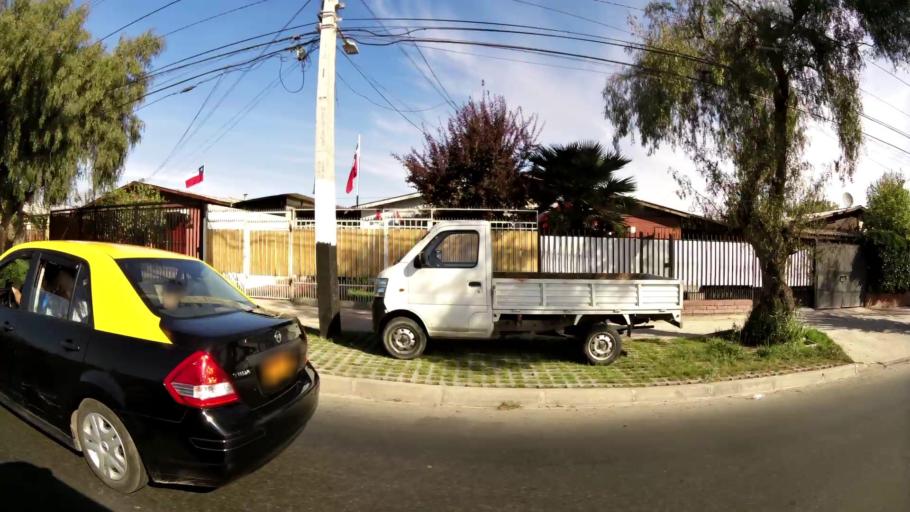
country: CL
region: Santiago Metropolitan
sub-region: Provincia de Cordillera
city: Puente Alto
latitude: -33.6063
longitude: -70.6022
